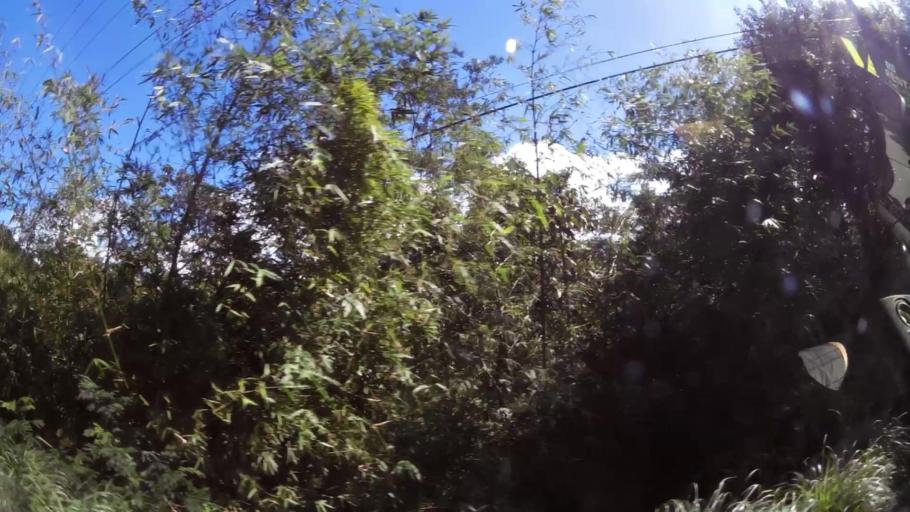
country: DM
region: Saint Paul
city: Pont Casse
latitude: 15.3464
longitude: -61.3633
